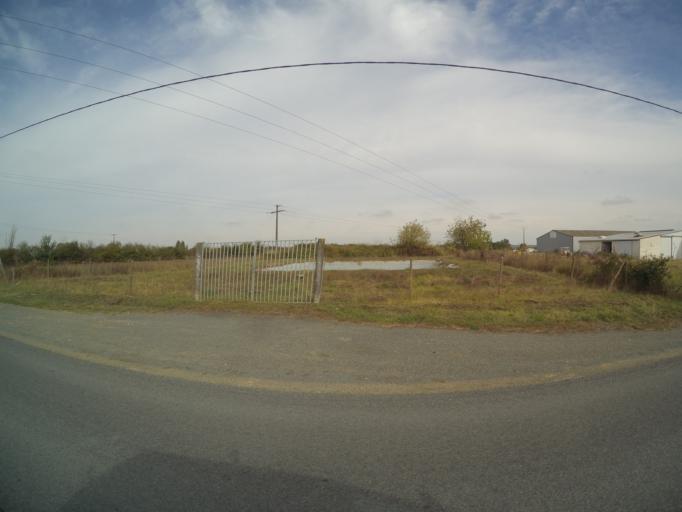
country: FR
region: Pays de la Loire
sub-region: Departement de Maine-et-Loire
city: Martigne-Briand
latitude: 47.2069
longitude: -0.4653
